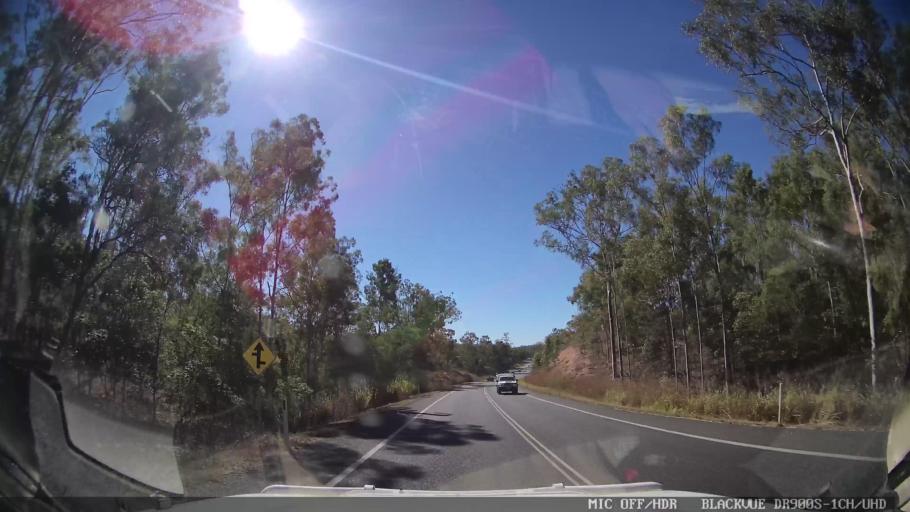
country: AU
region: Queensland
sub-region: Gladstone
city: Toolooa
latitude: -23.9635
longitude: 151.2175
